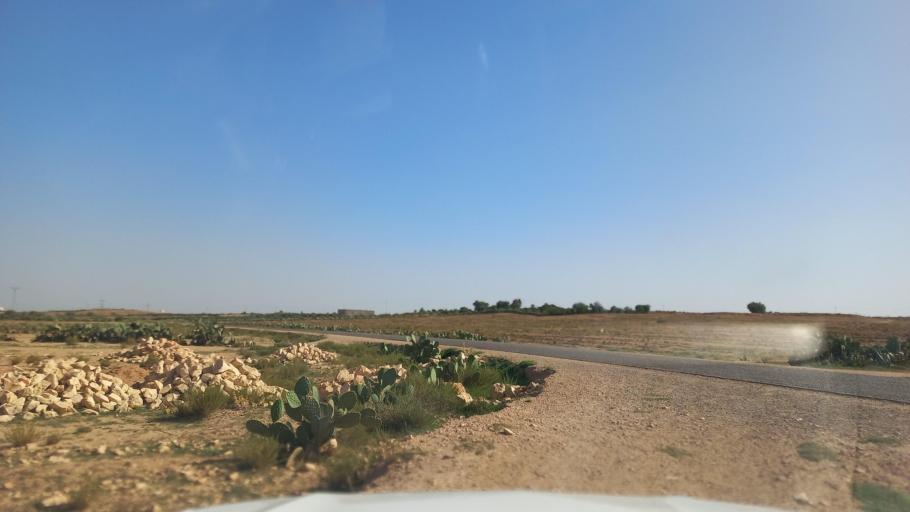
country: TN
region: Al Qasrayn
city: Sbiba
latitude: 35.3148
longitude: 9.0222
